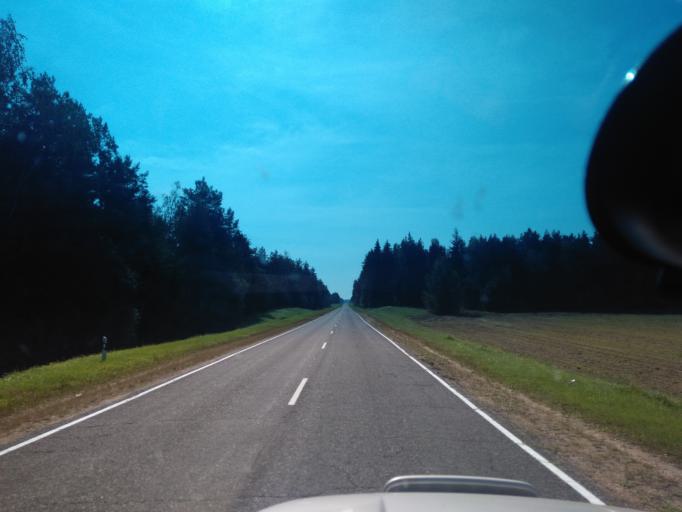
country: BY
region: Minsk
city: Uzda
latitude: 53.3324
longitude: 27.2303
